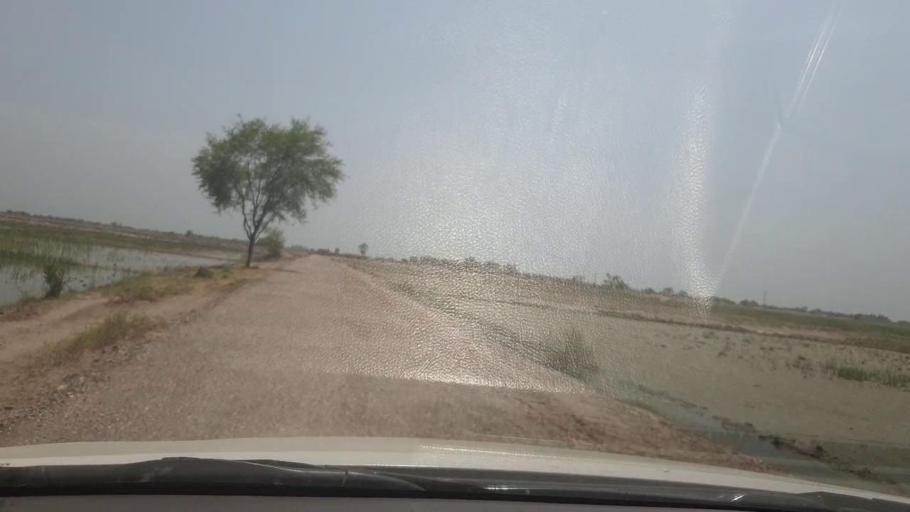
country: PK
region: Sindh
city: Shikarpur
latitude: 28.0309
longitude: 68.5715
